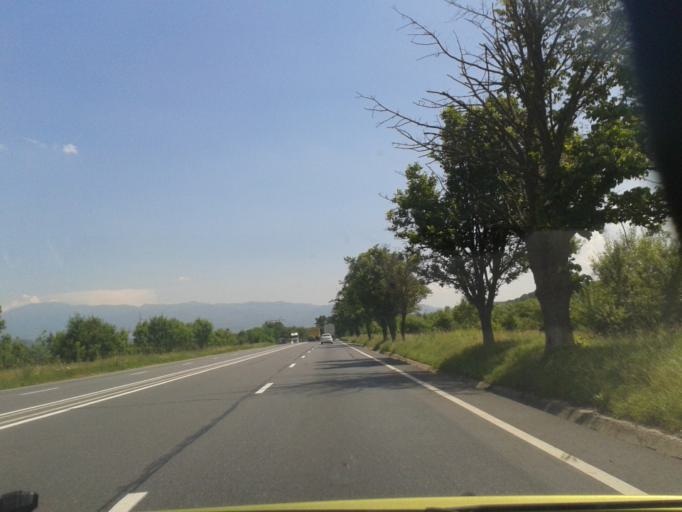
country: RO
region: Sibiu
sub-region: Comuna Selimbar
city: Selimbar
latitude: 45.7408
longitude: 24.2068
